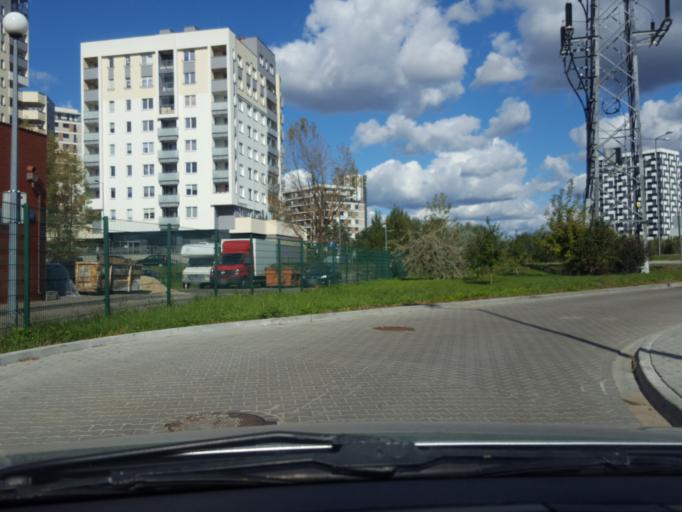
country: PL
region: Masovian Voivodeship
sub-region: Warszawa
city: Praga Poludnie
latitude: 52.2279
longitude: 21.1100
